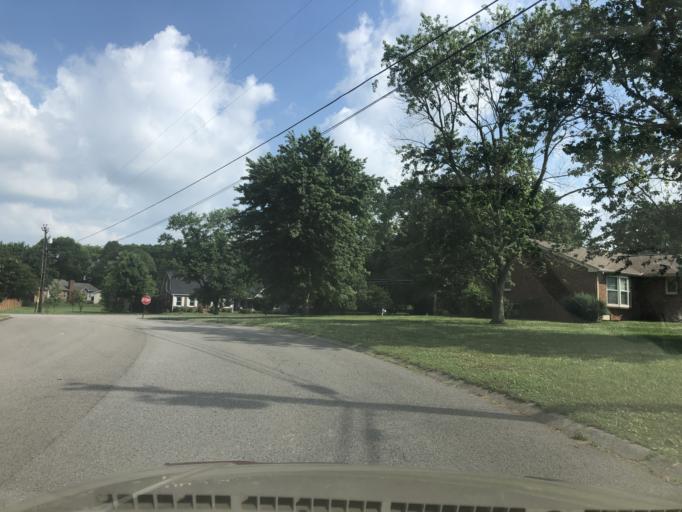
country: US
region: Tennessee
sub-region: Wilson County
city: Green Hill
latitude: 36.2350
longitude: -86.5829
